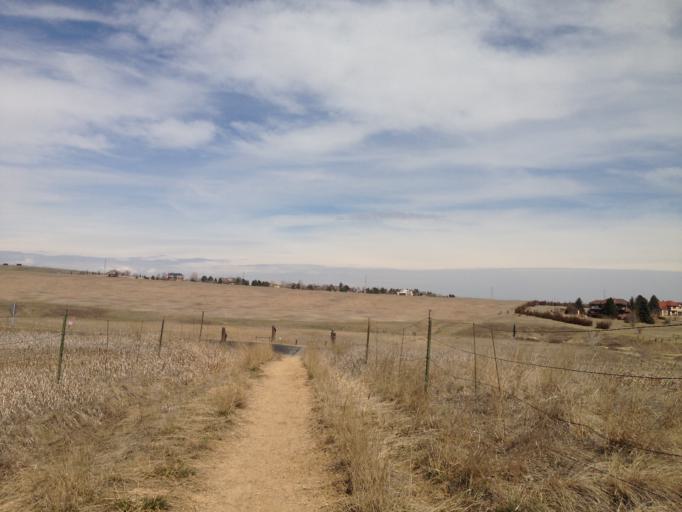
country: US
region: Colorado
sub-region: Boulder County
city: Gunbarrel
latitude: 40.0612
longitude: -105.1407
